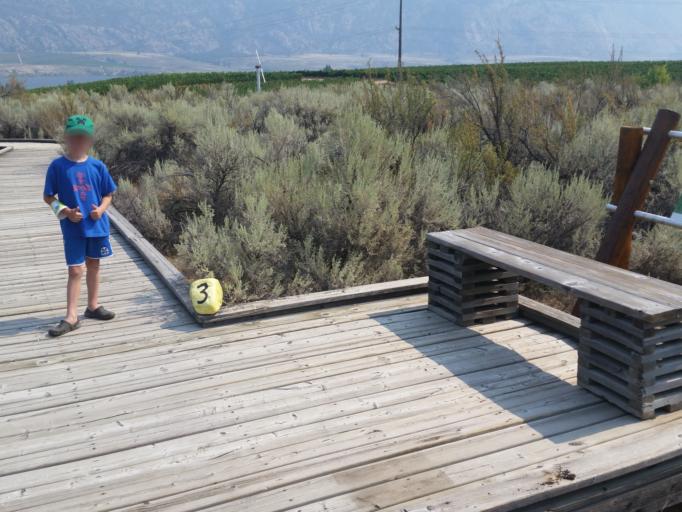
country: CA
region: British Columbia
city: Osoyoos
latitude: 49.0505
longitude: -119.5134
